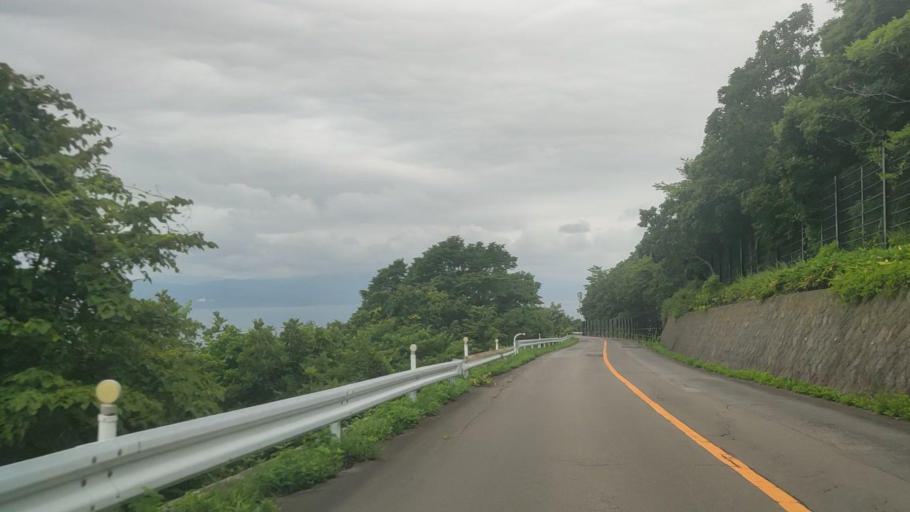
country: JP
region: Hokkaido
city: Hakodate
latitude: 41.7608
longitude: 140.6996
